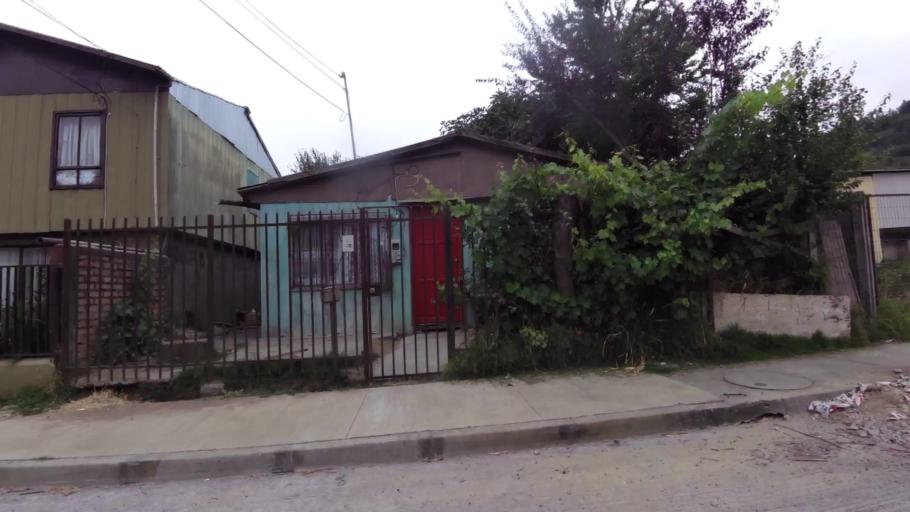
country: CL
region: Biobio
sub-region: Provincia de Concepcion
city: Concepcion
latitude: -36.8333
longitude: -73.0111
